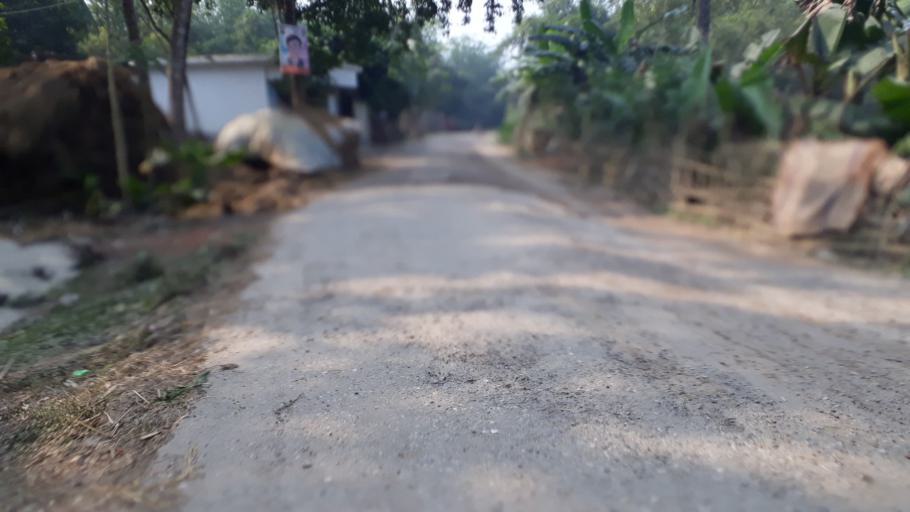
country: IN
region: West Bengal
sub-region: Nadia
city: Bagula
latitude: 23.3489
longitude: 88.8928
